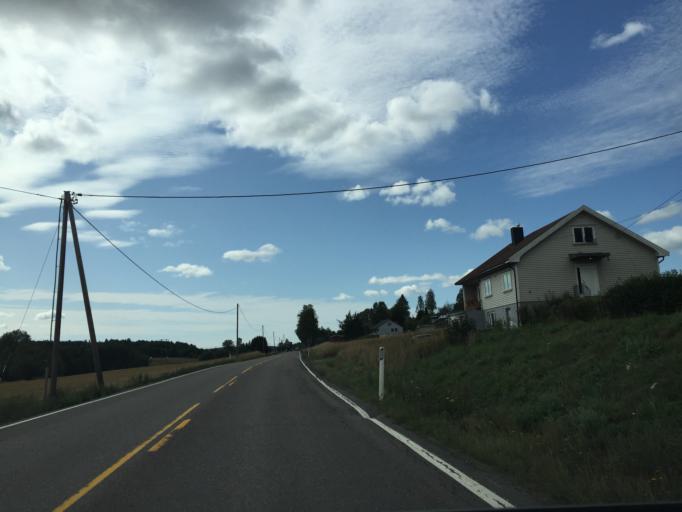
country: NO
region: Ostfold
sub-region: Hobol
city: Elvestad
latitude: 59.6132
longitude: 10.9318
